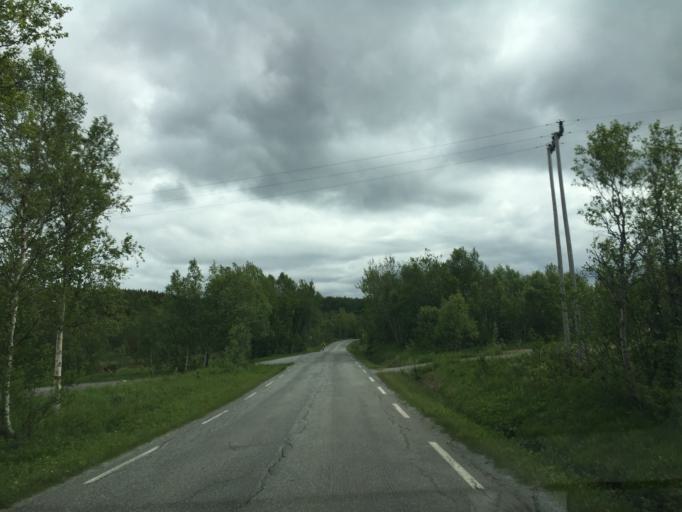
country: NO
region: Nordland
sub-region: Bodo
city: Loding
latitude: 67.3140
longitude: 14.6384
